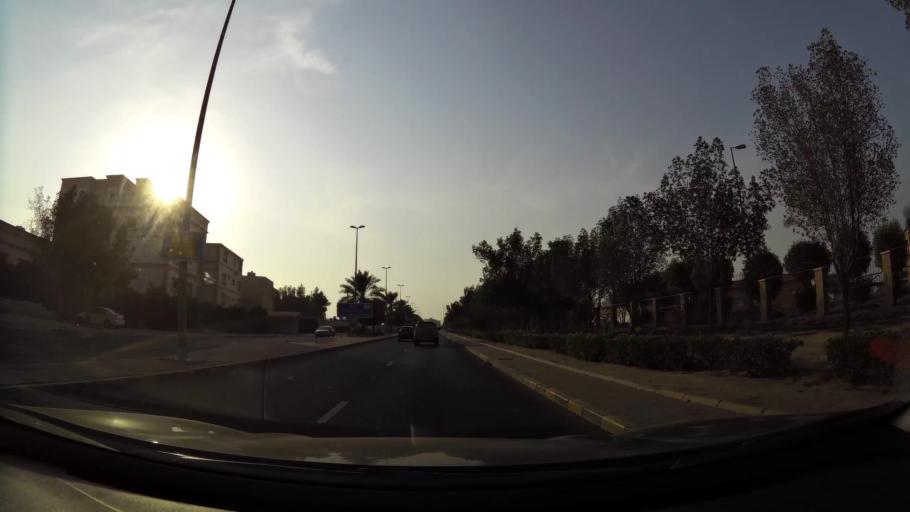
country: KW
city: Al Funaytis
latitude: 29.2214
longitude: 48.0703
